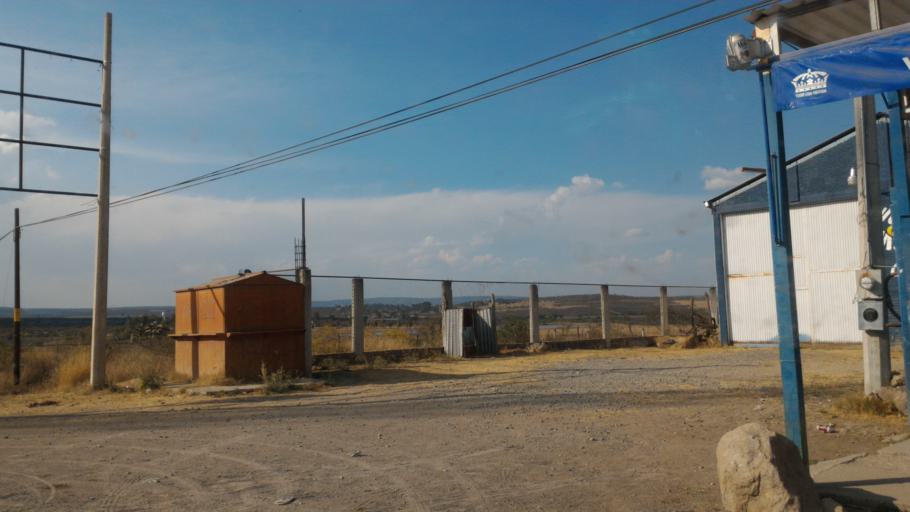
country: MX
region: Guanajuato
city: Ciudad Manuel Doblado
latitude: 20.8038
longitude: -101.9942
